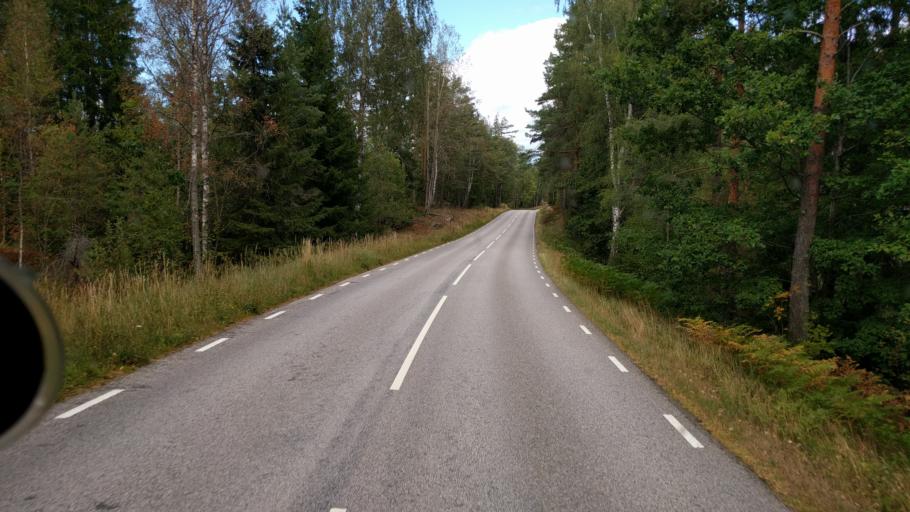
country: SE
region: Kalmar
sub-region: Vasterviks Kommun
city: Ankarsrum
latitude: 57.7665
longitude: 16.1370
